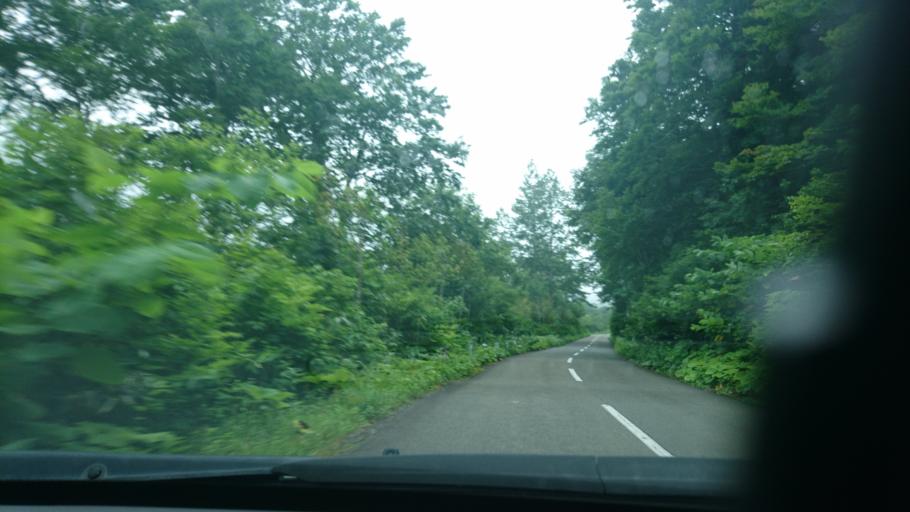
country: JP
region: Akita
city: Yuzawa
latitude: 39.1403
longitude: 140.7717
